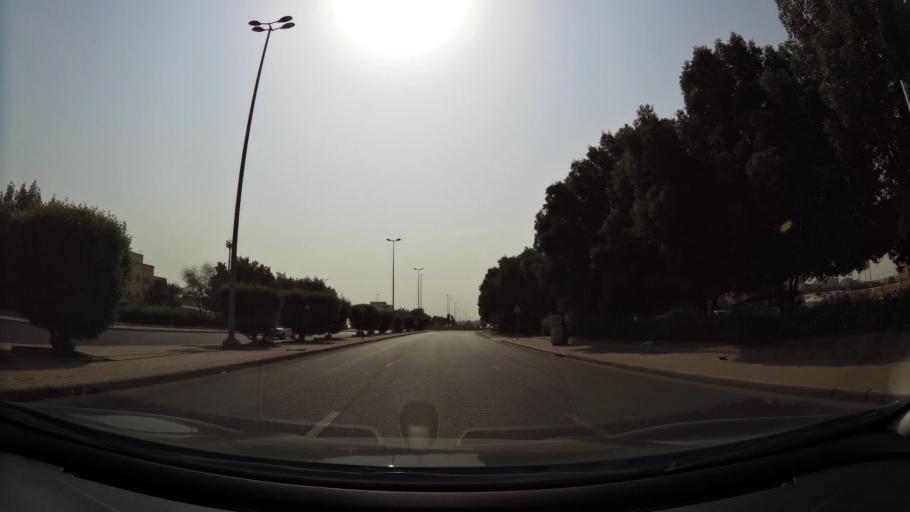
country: KW
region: Al Asimah
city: Ar Rabiyah
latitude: 29.2824
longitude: 47.8862
